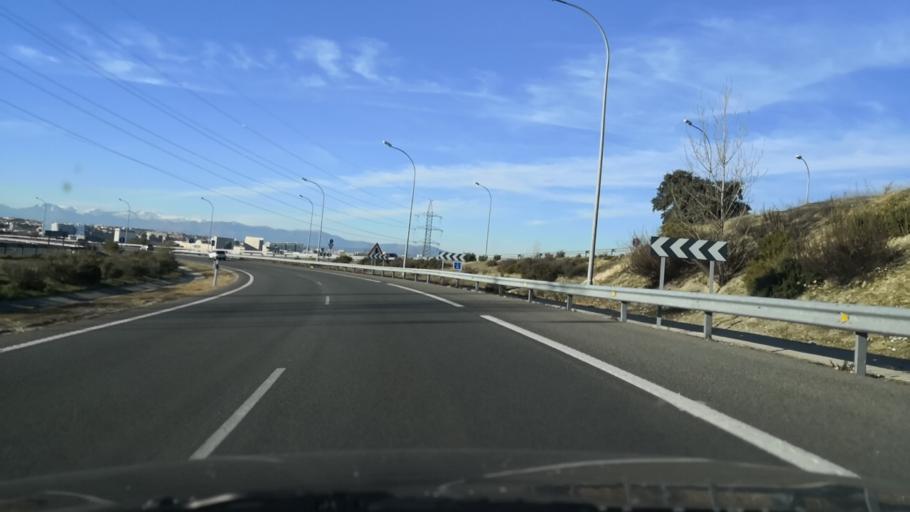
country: ES
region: Madrid
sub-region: Provincia de Madrid
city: San Sebastian de los Reyes
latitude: 40.5260
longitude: -3.5990
